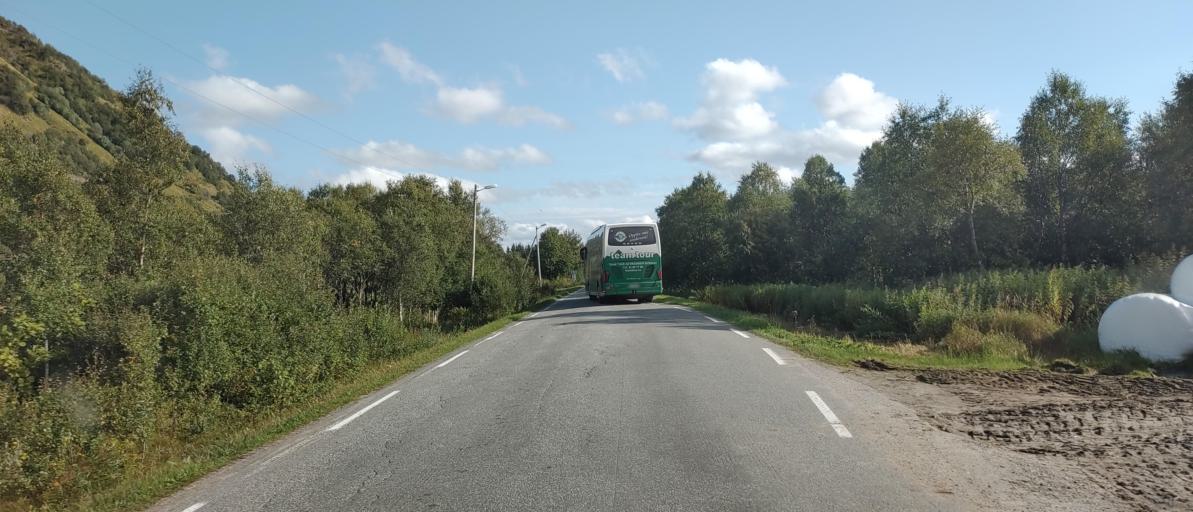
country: NO
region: Nordland
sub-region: Sortland
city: Sortland
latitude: 69.0358
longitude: 15.5232
